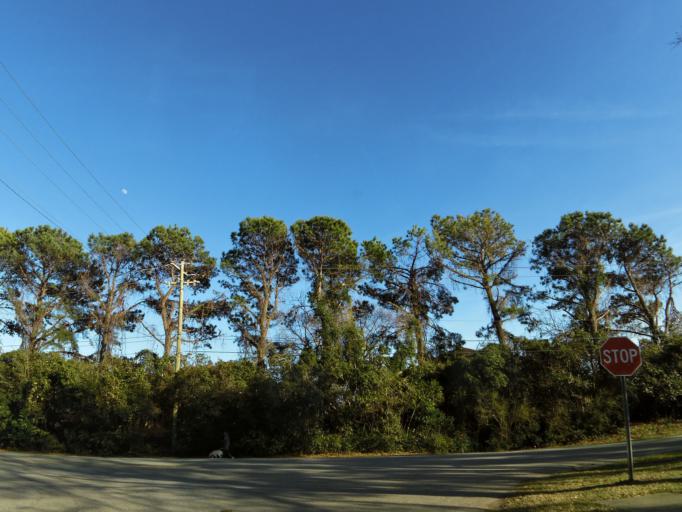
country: US
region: South Carolina
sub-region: Charleston County
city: Mount Pleasant
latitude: 32.8011
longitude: -79.8950
